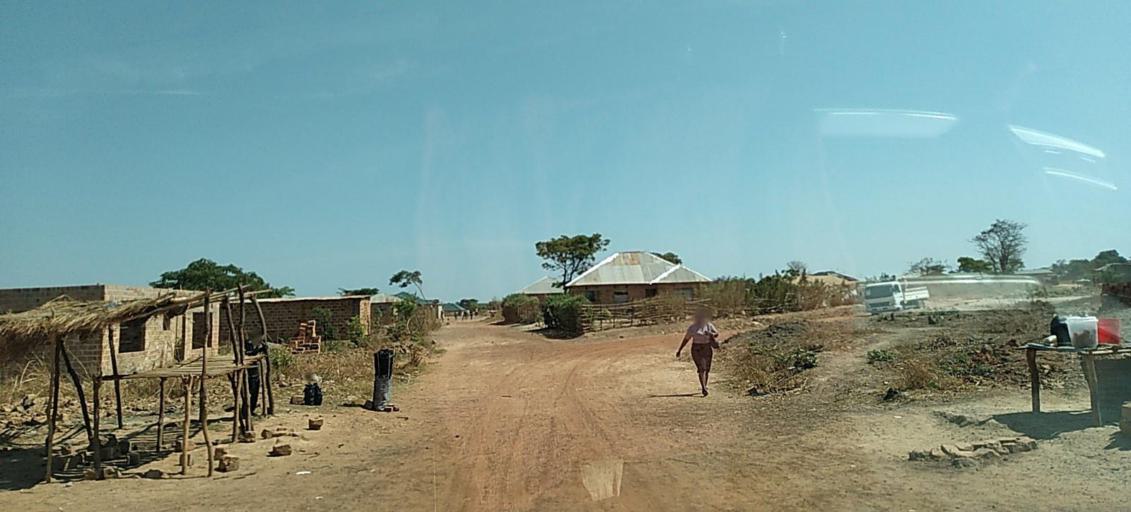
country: ZM
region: Copperbelt
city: Chililabombwe
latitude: -12.3212
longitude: 27.8603
